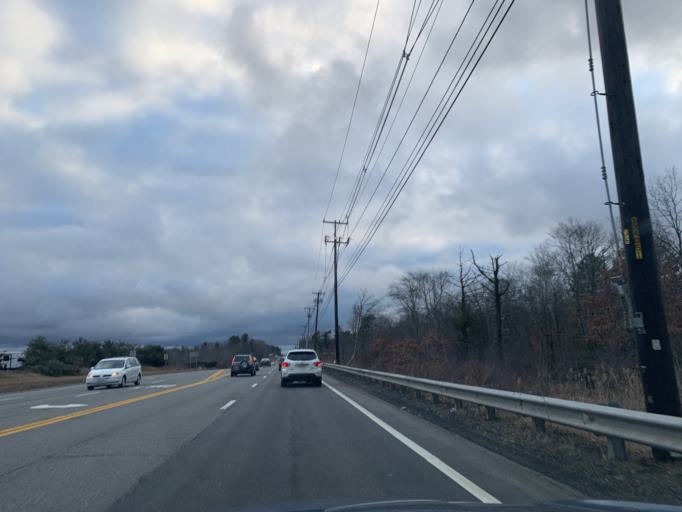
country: US
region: Massachusetts
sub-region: Norfolk County
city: Wrentham
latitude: 42.0542
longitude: -71.2991
